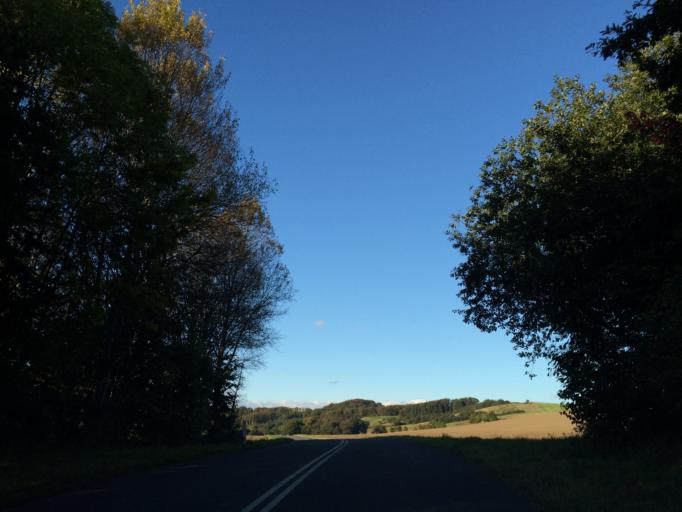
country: DK
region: Central Jutland
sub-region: Skanderborg Kommune
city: Ry
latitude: 56.1143
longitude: 9.7340
